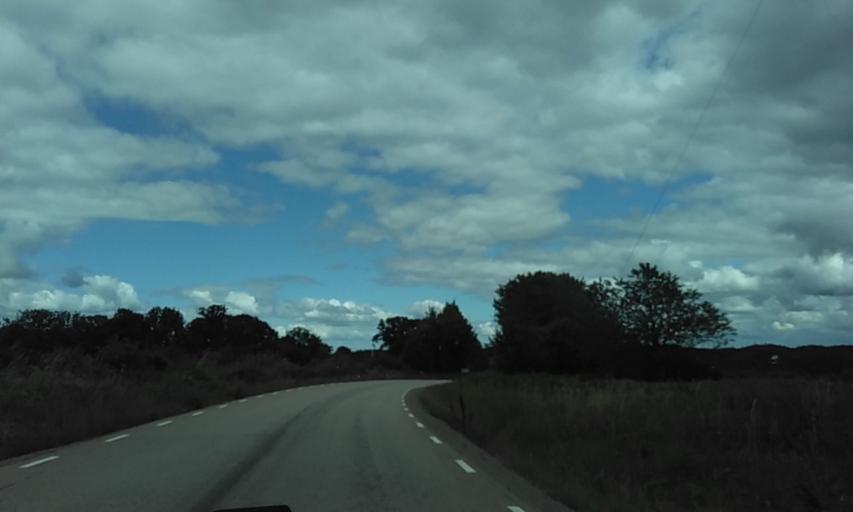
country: SE
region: Vaestra Goetaland
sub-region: Boras Kommun
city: Boras
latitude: 57.8031
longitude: 12.8971
